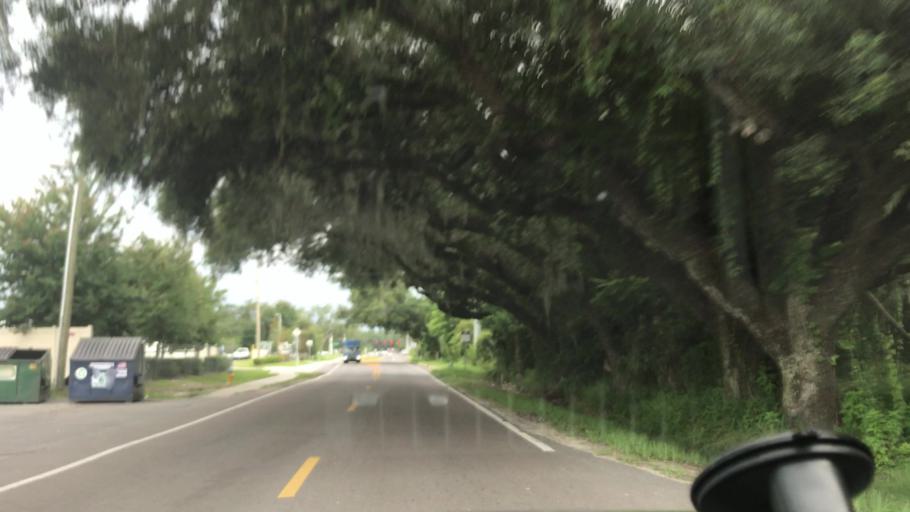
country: US
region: Florida
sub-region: Hillsborough County
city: Mango
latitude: 27.9851
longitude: -82.3188
